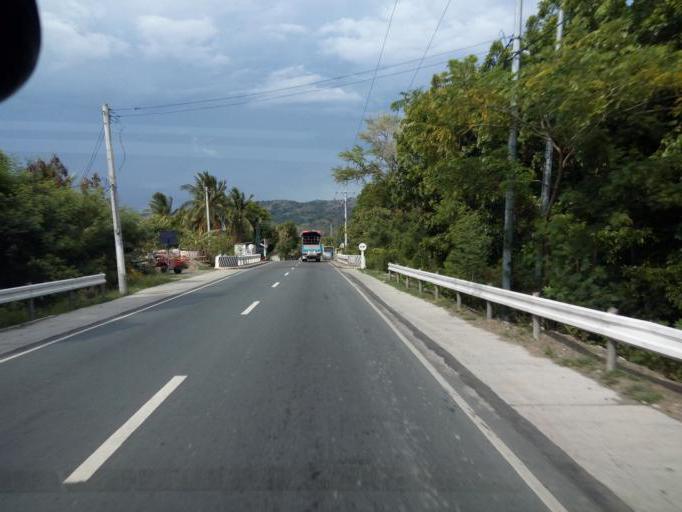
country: PH
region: Central Luzon
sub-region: Province of Nueva Ecija
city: Tayabo
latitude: 15.8267
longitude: 121.0209
